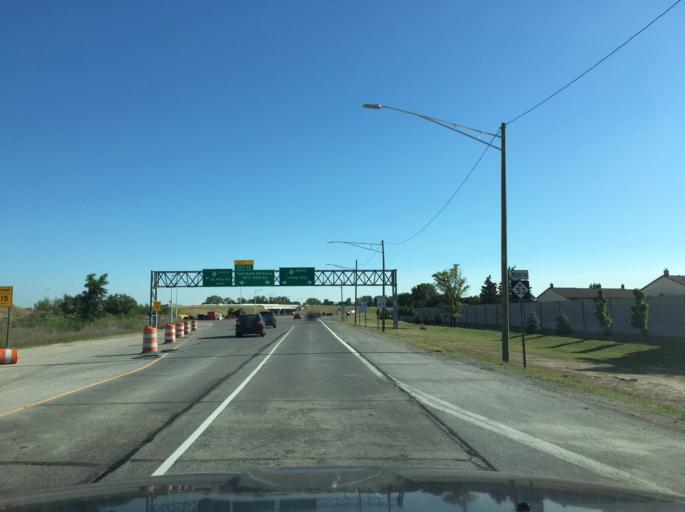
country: US
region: Michigan
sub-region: Macomb County
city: Sterling Heights
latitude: 42.5953
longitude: -83.0299
